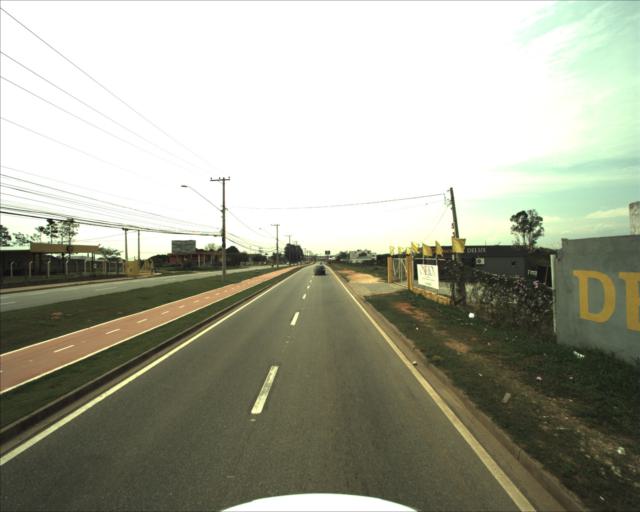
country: BR
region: Sao Paulo
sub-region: Sorocaba
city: Sorocaba
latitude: -23.4520
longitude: -47.4413
